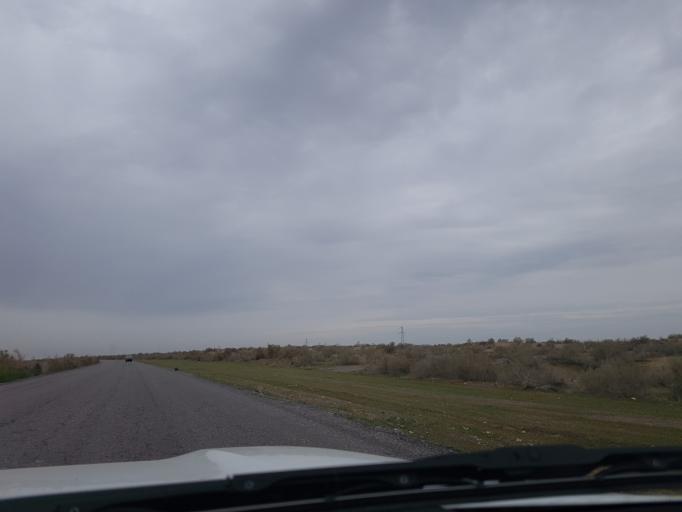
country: TM
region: Lebap
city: Turkmenabat
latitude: 38.8576
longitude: 63.4093
